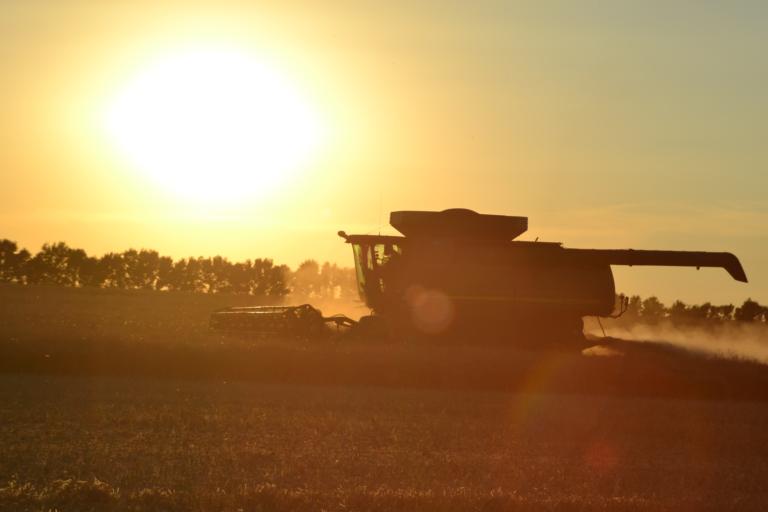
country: US
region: North Dakota
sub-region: Mercer County
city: Beulah
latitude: 47.6877
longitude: -101.9023
